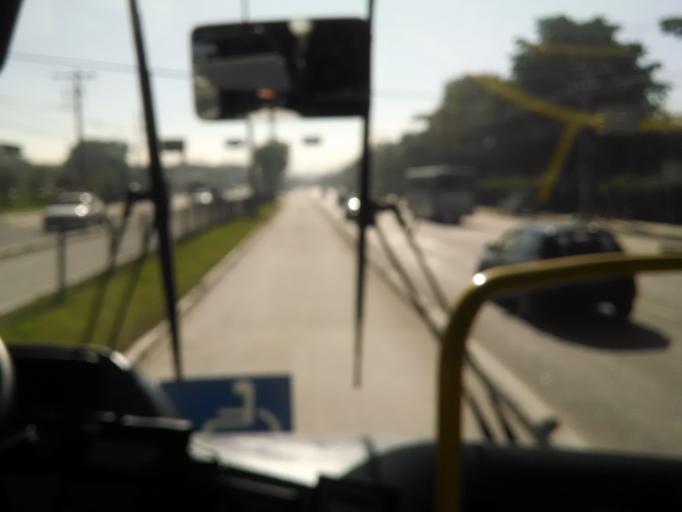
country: BR
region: Rio de Janeiro
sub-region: Sao Joao De Meriti
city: Sao Joao de Meriti
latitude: -22.9538
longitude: -43.3757
